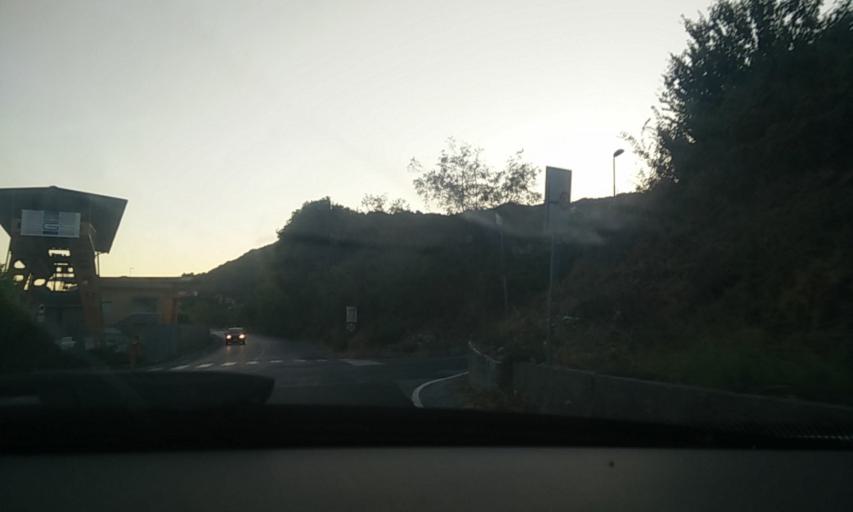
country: IT
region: Tuscany
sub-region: Provincia di Massa-Carrara
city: Carrara
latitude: 44.0724
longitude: 10.0883
